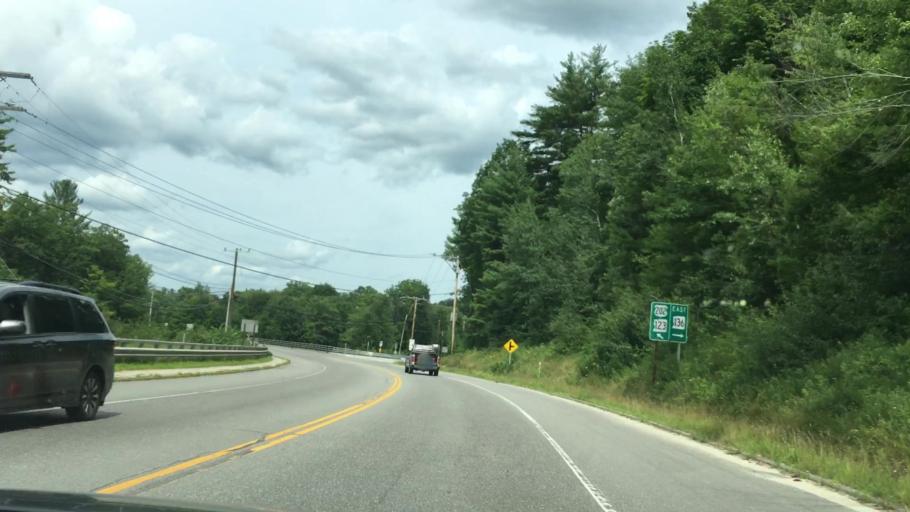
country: US
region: New Hampshire
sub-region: Hillsborough County
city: Peterborough
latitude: 42.8985
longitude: -71.9403
